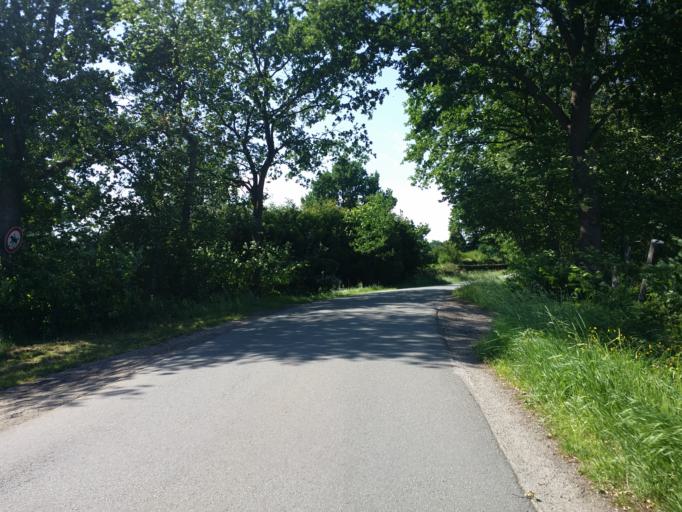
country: DE
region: Lower Saxony
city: Rastede
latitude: 53.2127
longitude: 8.2556
